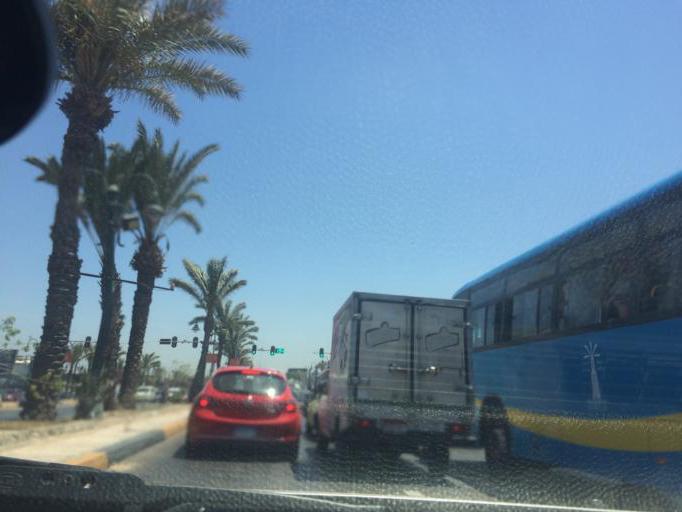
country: EG
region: Alexandria
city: Alexandria
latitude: 31.1747
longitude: 29.9316
